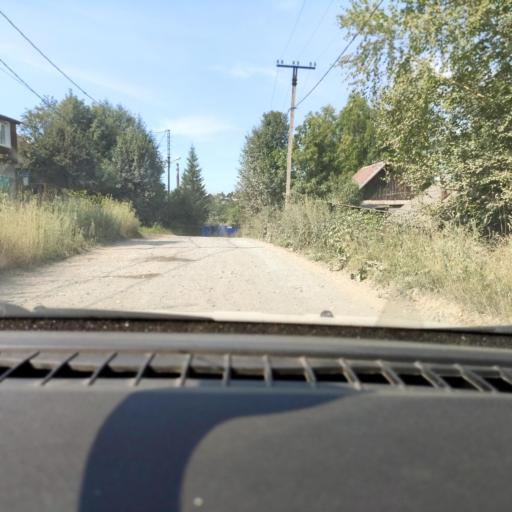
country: RU
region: Perm
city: Polazna
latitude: 58.1393
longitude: 56.4574
